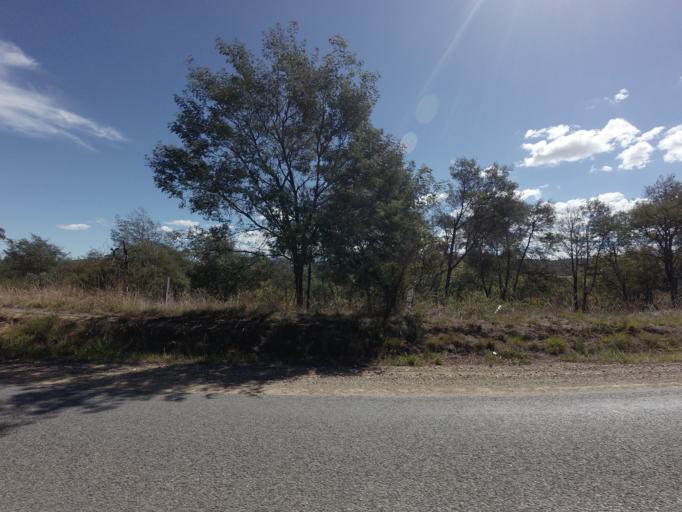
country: AU
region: Tasmania
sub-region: Break O'Day
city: St Helens
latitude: -41.6442
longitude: 147.9613
